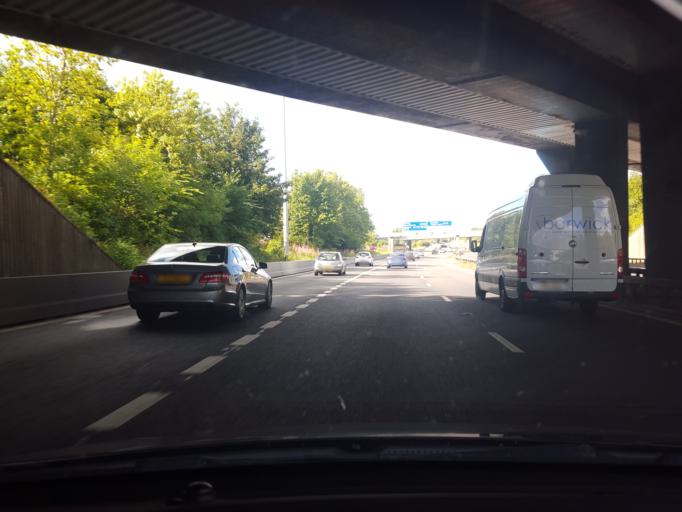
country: GB
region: Scotland
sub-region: South Lanarkshire
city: Uddingston
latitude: 55.8278
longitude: -4.0893
